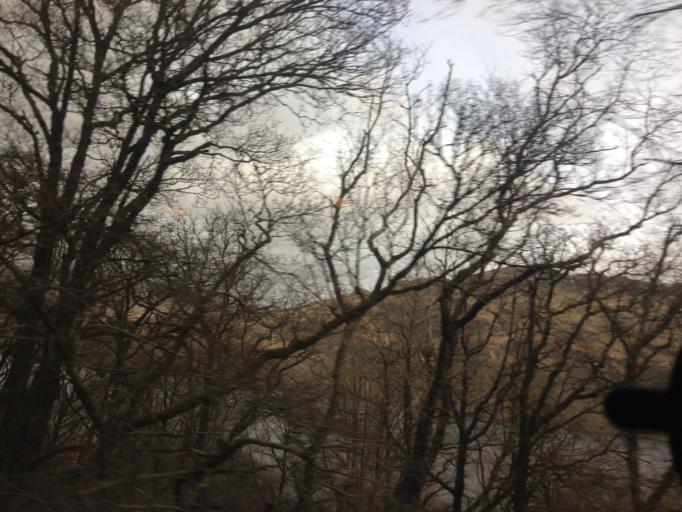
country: GB
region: Scotland
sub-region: Argyll and Bute
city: Garelochhead
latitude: 56.2237
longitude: -4.6985
